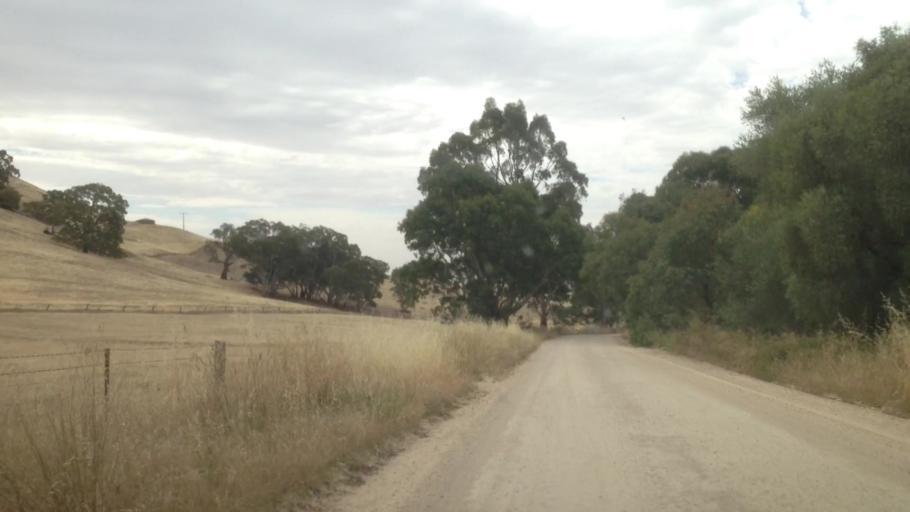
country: AU
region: South Australia
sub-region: Barossa
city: Lyndoch
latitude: -34.6058
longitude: 138.9495
